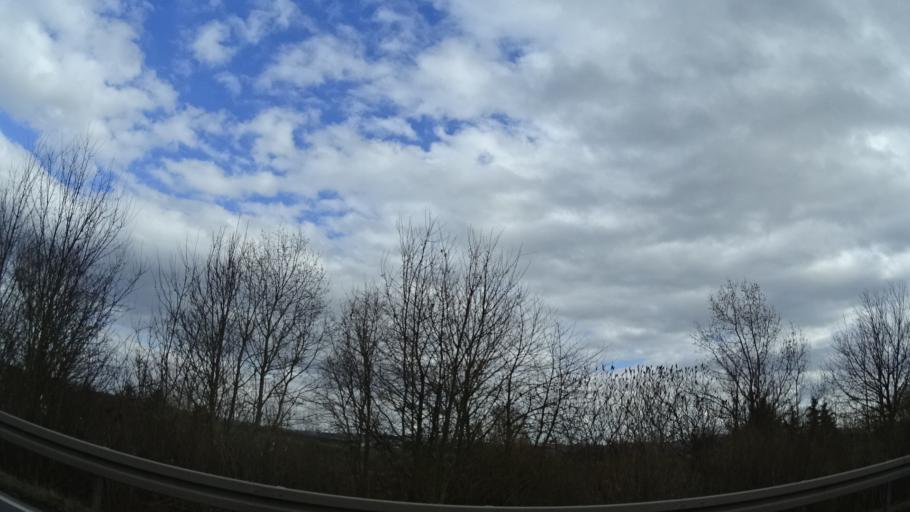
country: DE
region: Hesse
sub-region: Regierungsbezirk Darmstadt
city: Stockstadt am Rhein
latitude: 49.7967
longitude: 8.4843
